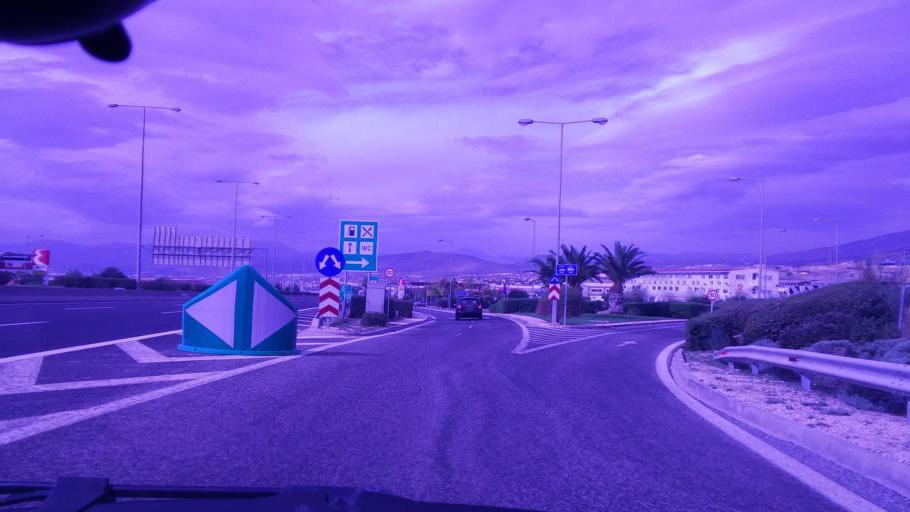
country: GR
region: Attica
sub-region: Nomarchia Dytikis Attikis
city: Aspropyrgos
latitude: 38.0928
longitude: 23.6074
